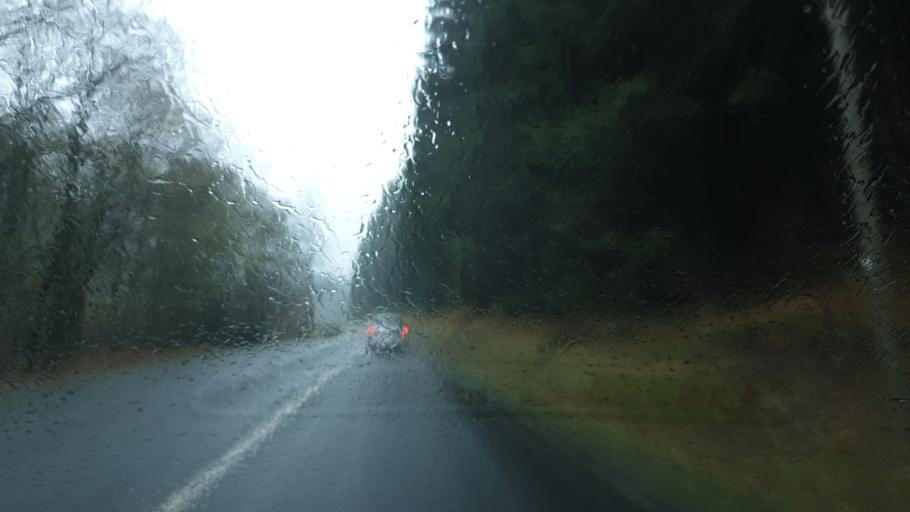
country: DE
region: Saxony
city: Tannenbergsthal
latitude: 50.4235
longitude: 12.4718
